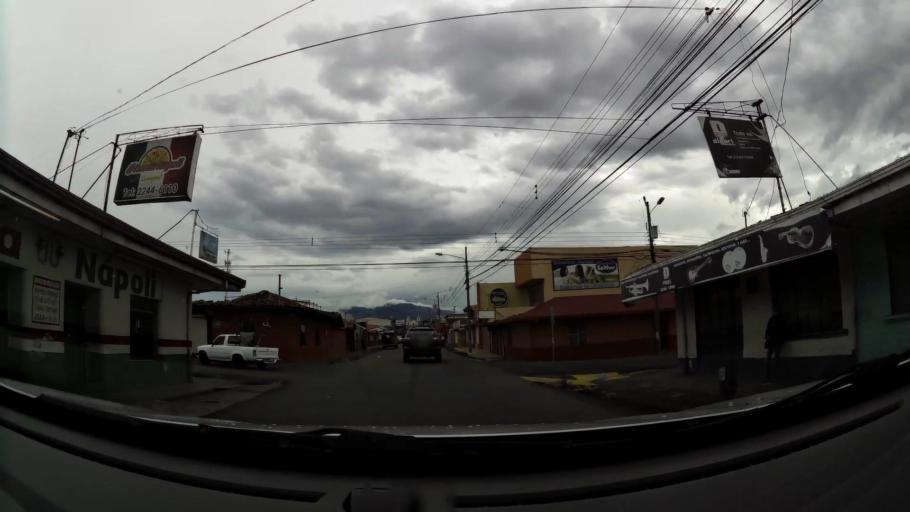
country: CR
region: Heredia
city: San Pablo
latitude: 9.9823
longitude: -84.0933
